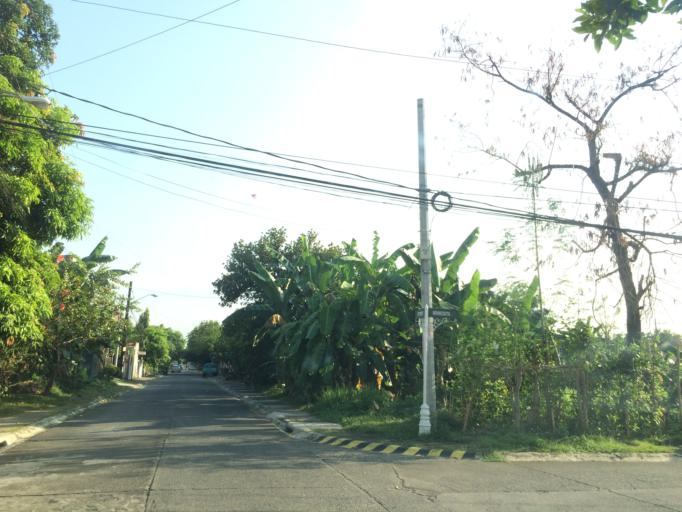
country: PH
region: Calabarzon
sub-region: Province of Rizal
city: San Mateo
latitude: 14.6721
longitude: 121.1230
